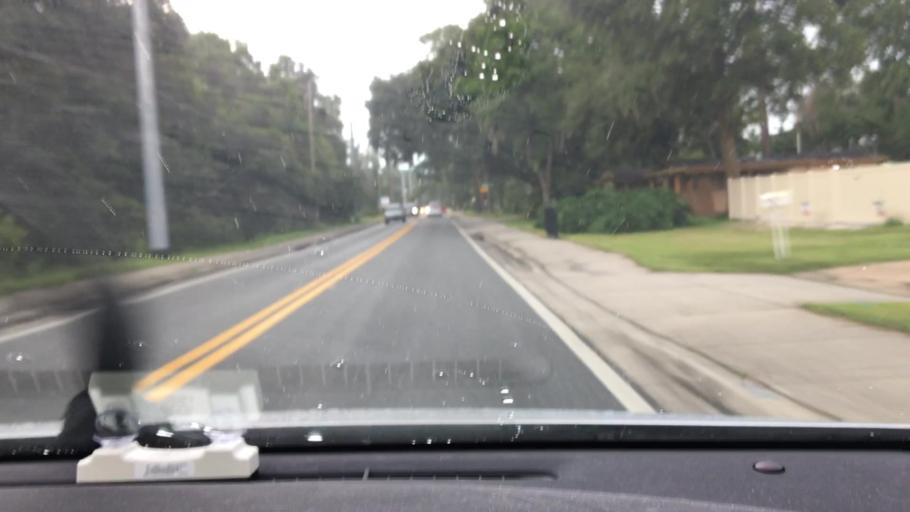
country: US
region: Florida
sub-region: Seminole County
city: Casselberry
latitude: 28.6706
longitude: -81.3458
